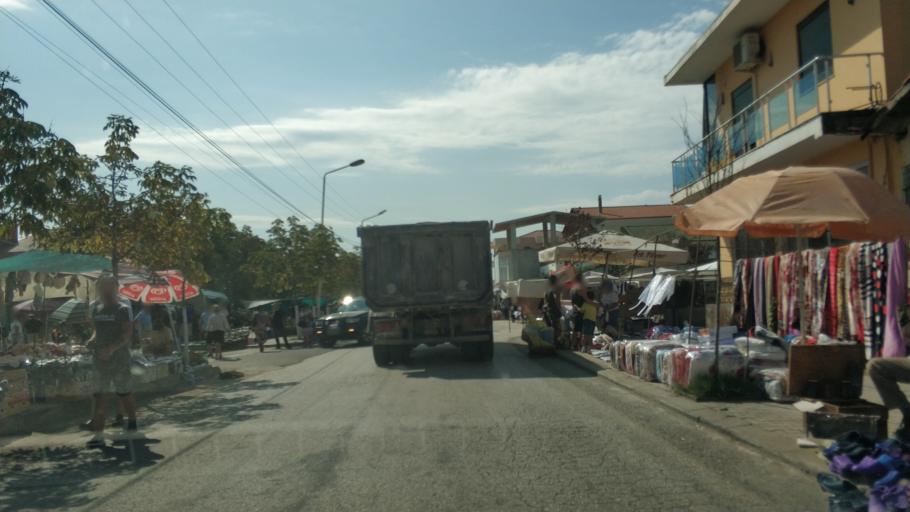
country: AL
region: Fier
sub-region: Rrethi i Lushnjes
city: Divjake
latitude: 40.9941
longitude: 19.5332
